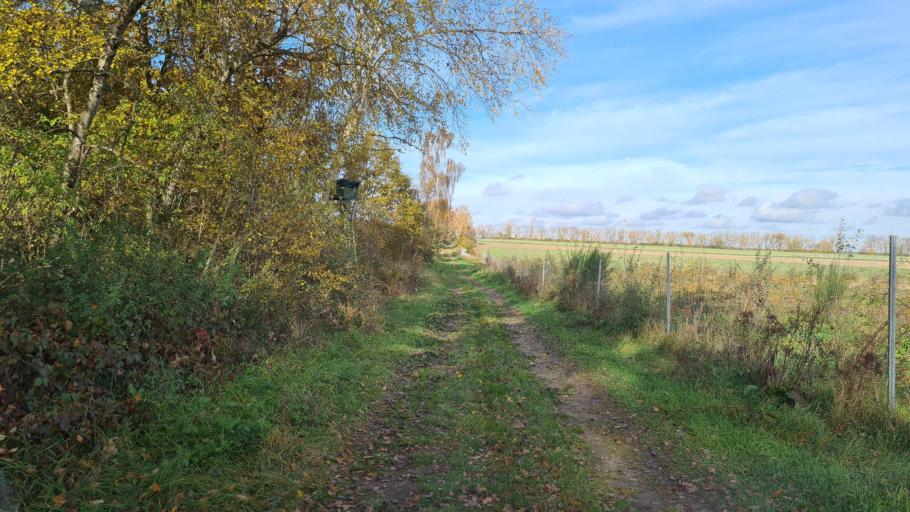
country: DE
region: Saxony-Anhalt
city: Zahna
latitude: 51.9682
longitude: 12.8391
